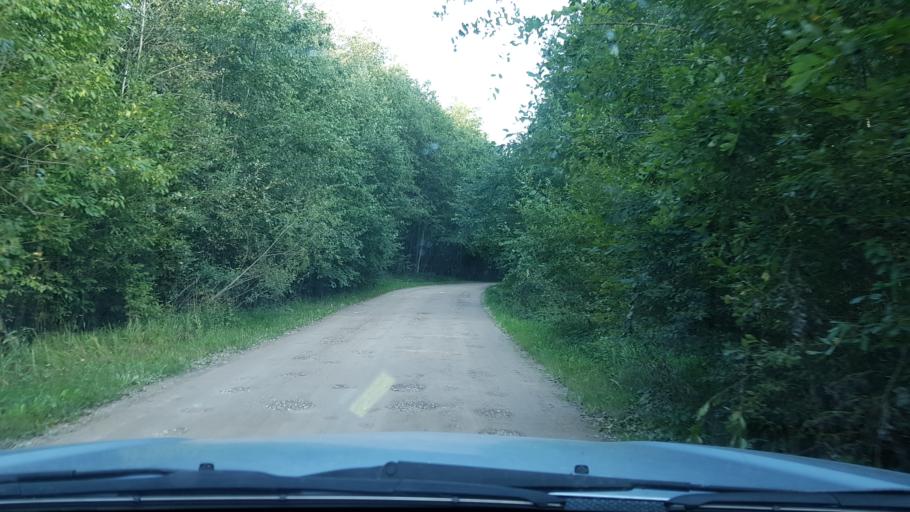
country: EE
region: Ida-Virumaa
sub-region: Sillamaee linn
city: Sillamae
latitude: 59.2742
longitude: 27.9209
